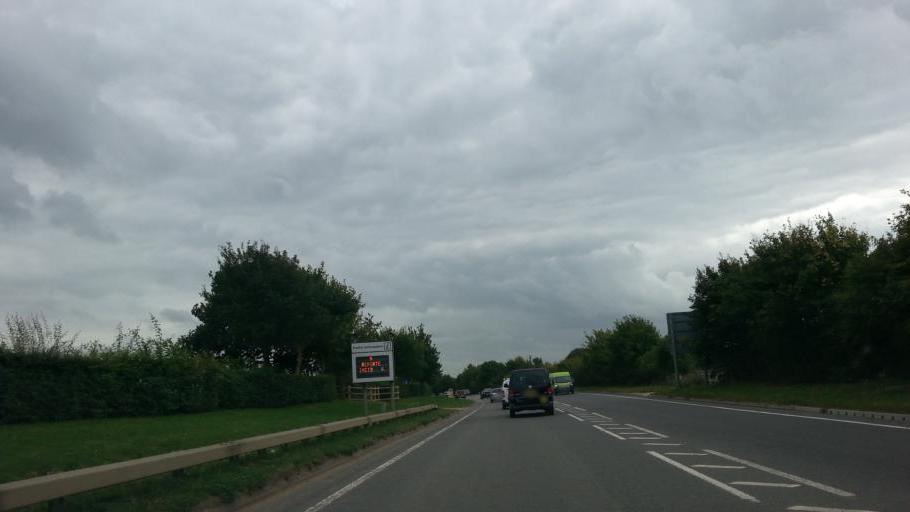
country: GB
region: England
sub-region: Essex
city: Chelmsford
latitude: 51.7632
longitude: 0.4889
